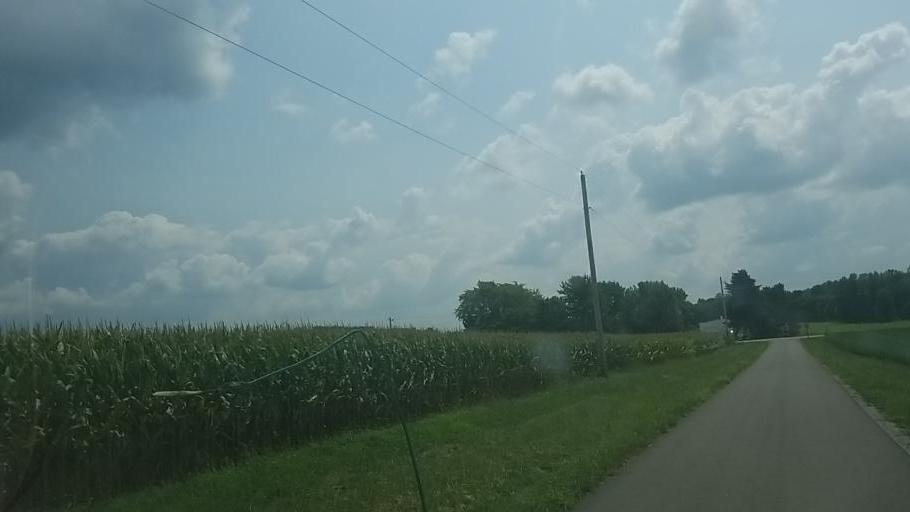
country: US
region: Ohio
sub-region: Wyandot County
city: Carey
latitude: 40.9649
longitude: -83.2855
